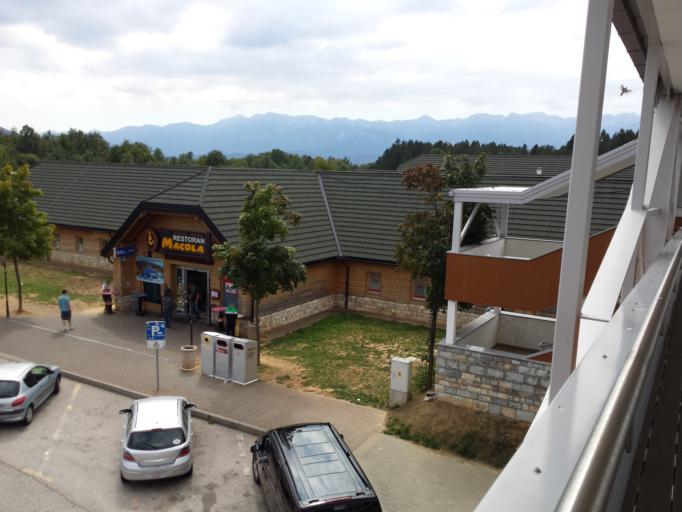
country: HR
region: Zadarska
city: Starigrad
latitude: 44.4620
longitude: 15.6019
